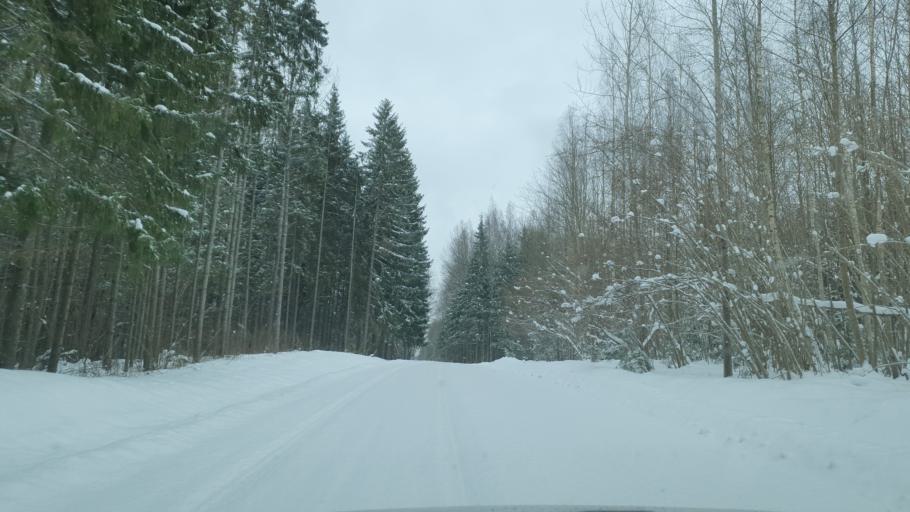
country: EE
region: Polvamaa
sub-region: Raepina vald
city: Rapina
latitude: 58.1969
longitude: 27.3286
